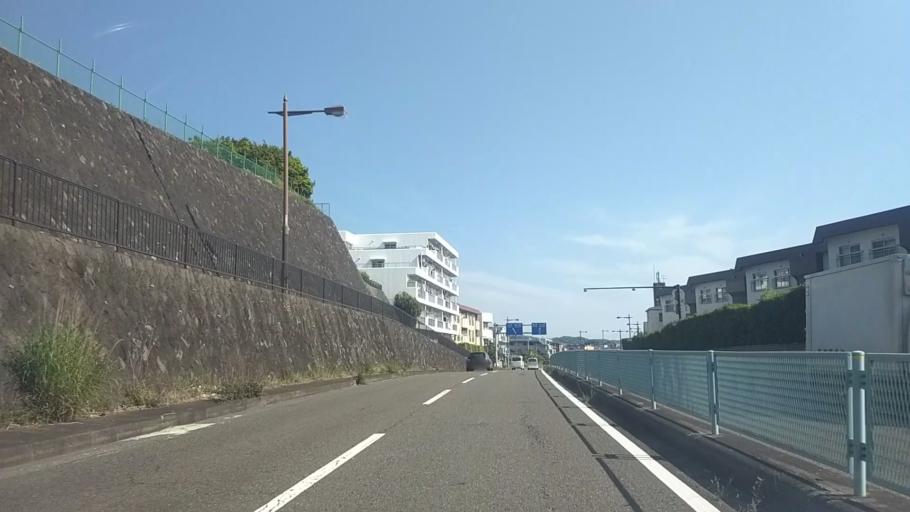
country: JP
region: Kanagawa
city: Fujisawa
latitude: 35.3435
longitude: 139.5016
